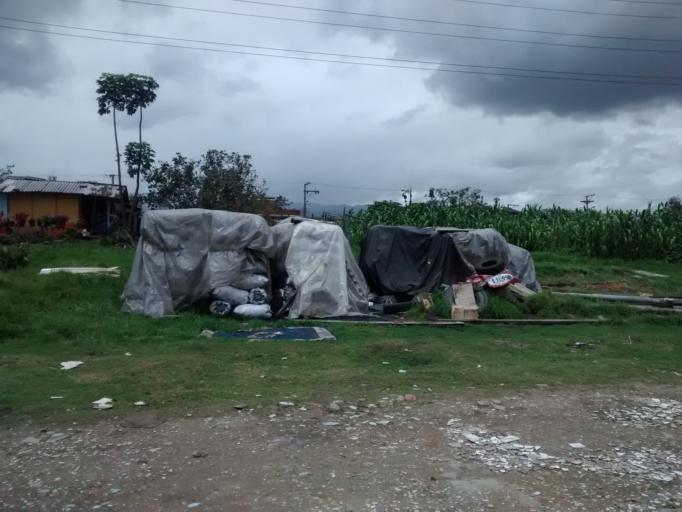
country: CO
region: Bogota D.C.
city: Bogota
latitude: 4.6985
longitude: -74.1157
